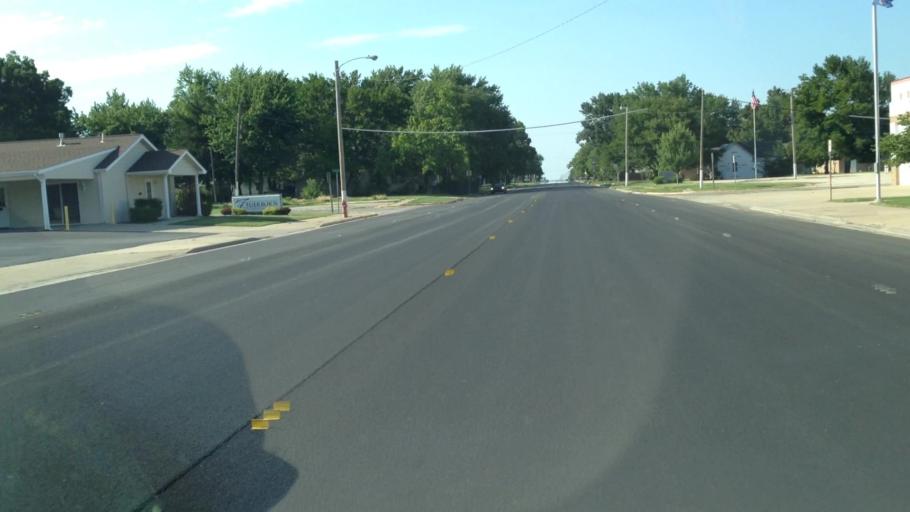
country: US
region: Kansas
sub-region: Allen County
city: Iola
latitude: 37.9161
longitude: -95.1701
